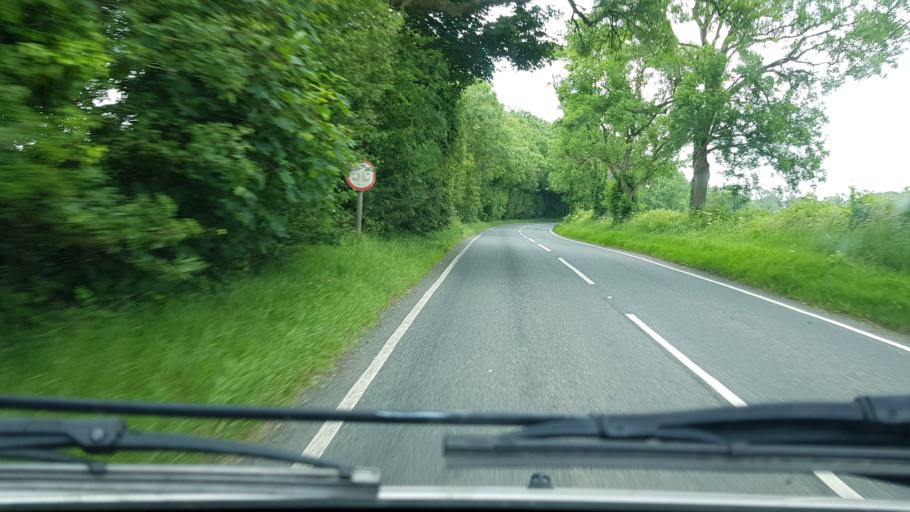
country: GB
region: England
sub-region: Gloucestershire
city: Donnington
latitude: 51.9521
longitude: -1.7445
